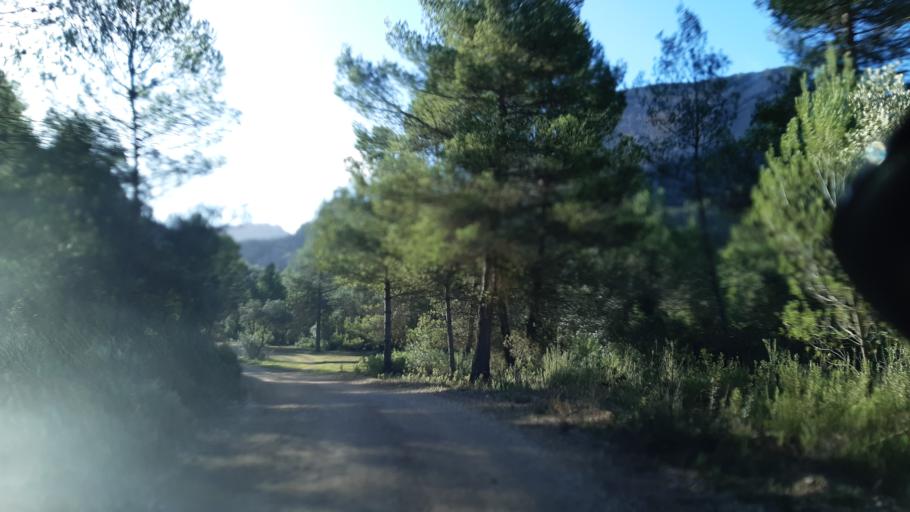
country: ES
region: Aragon
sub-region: Provincia de Teruel
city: Lledo
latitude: 40.8618
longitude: 0.2533
